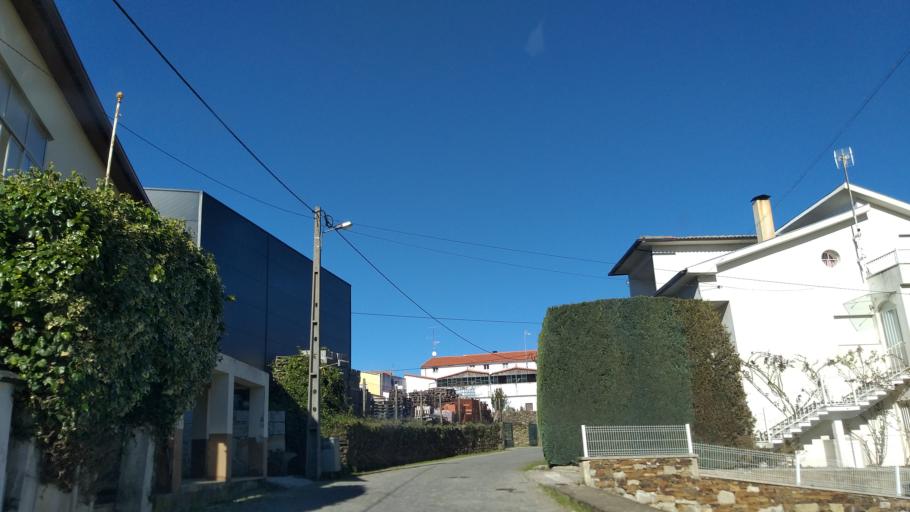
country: PT
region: Guarda
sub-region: Celorico da Beira
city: Celorico da Beira
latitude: 40.5134
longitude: -7.3929
